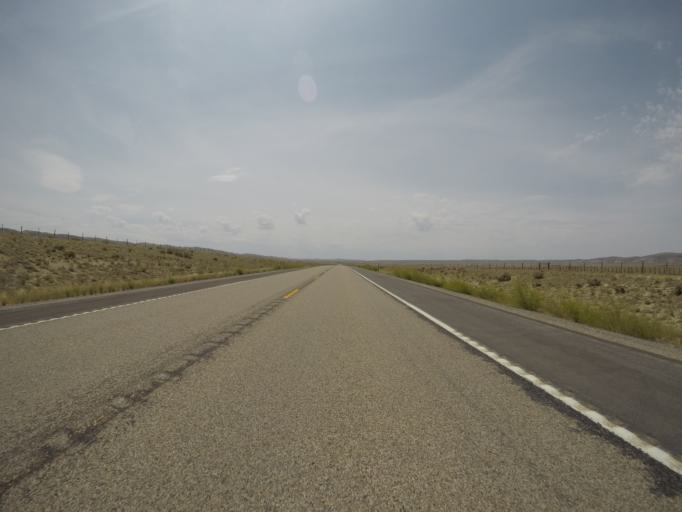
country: US
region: Wyoming
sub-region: Lincoln County
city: Kemmerer
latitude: 41.6611
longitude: -110.5700
